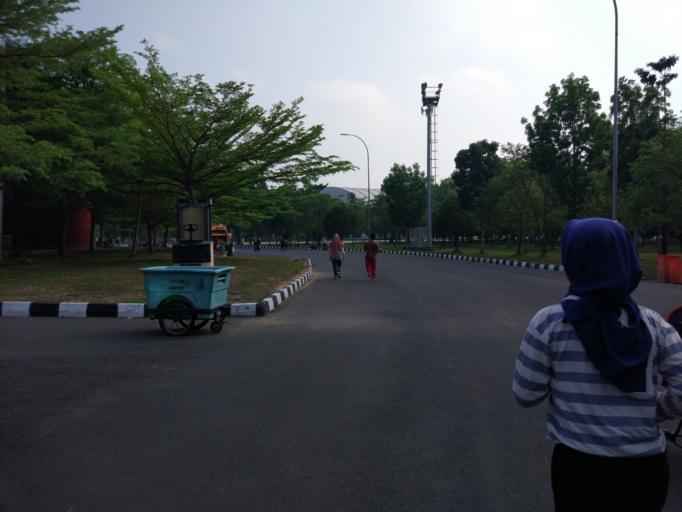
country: ID
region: South Sumatra
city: Plaju
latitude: -3.0224
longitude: 104.7898
